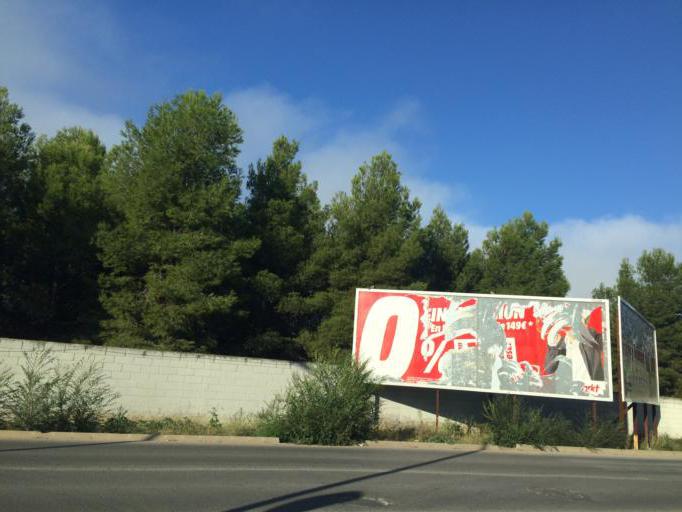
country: ES
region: Castille-La Mancha
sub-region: Provincia de Albacete
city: Albacete
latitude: 39.0033
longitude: -1.8704
